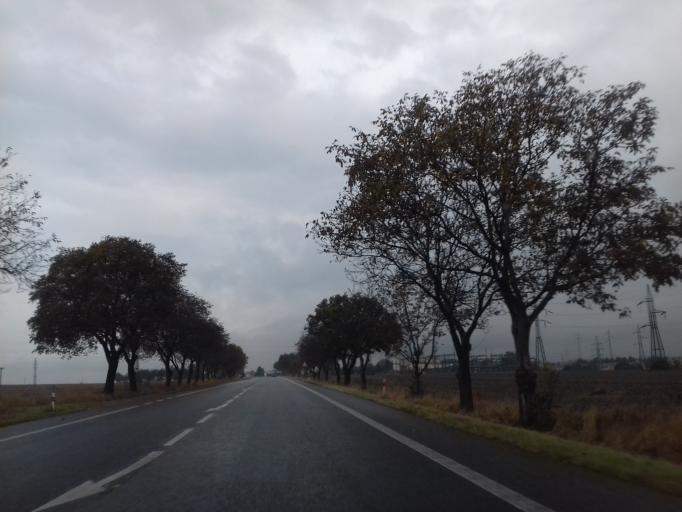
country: CZ
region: Kralovehradecky
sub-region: Okres Hradec Kralove
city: Vsestary
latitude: 50.2473
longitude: 15.7706
